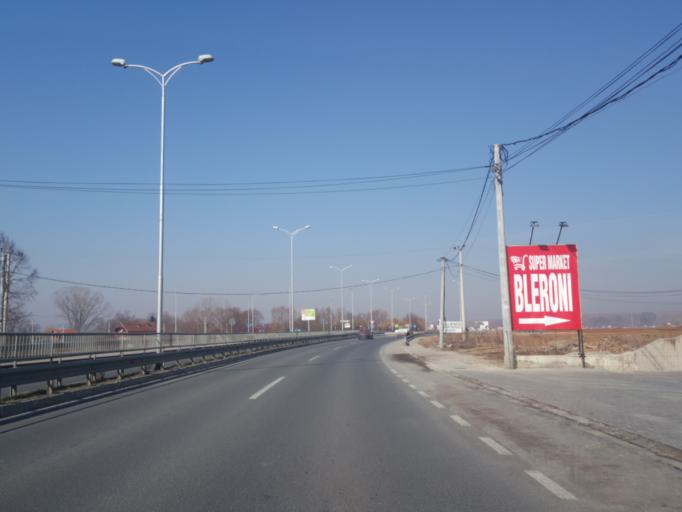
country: XK
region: Pristina
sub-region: Komuna e Obiliqit
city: Obiliq
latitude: 42.7247
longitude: 21.0810
